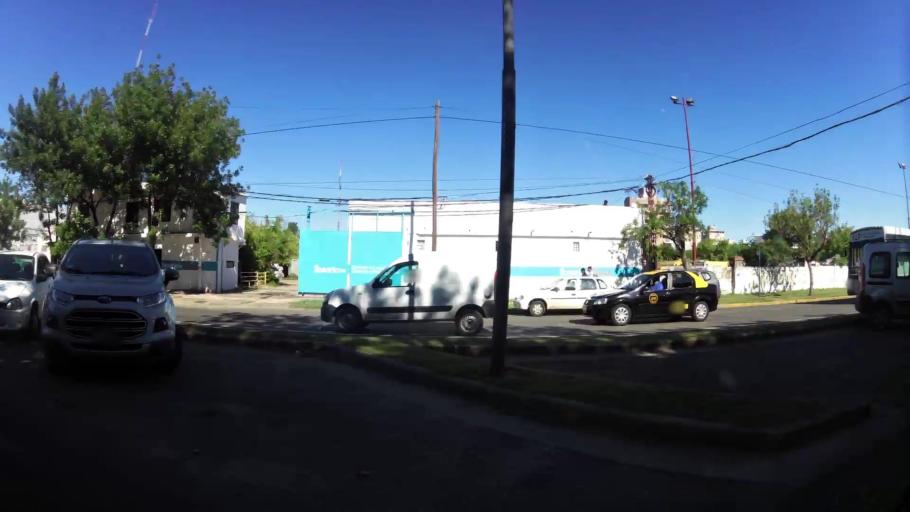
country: AR
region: Santa Fe
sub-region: Departamento de Rosario
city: Rosario
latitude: -32.9547
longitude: -60.6689
